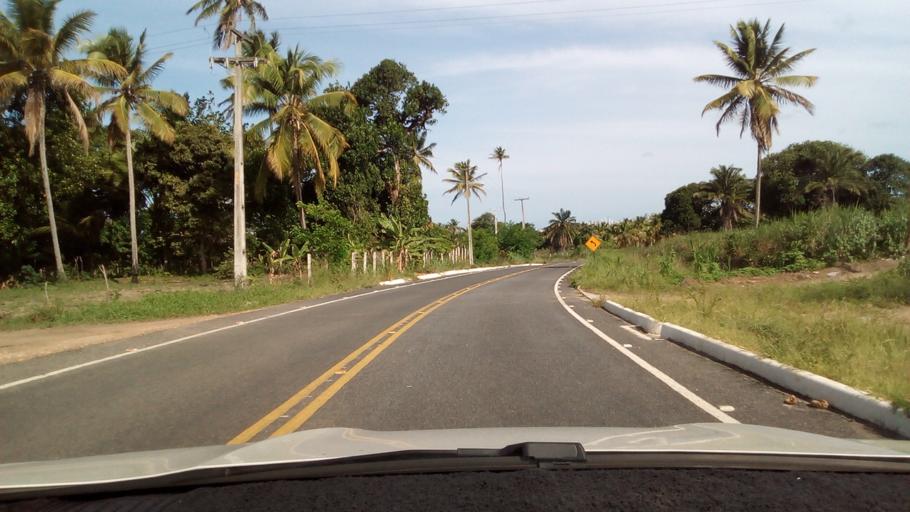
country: BR
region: Paraiba
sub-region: Bayeux
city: Bayeux
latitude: -7.0510
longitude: -34.9088
